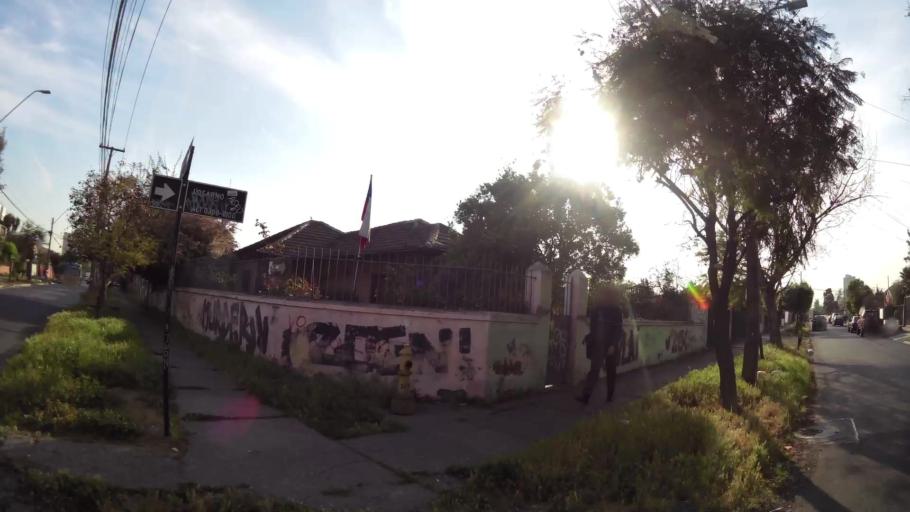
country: CL
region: Santiago Metropolitan
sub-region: Provincia de Santiago
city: Santiago
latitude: -33.5177
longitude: -70.6635
